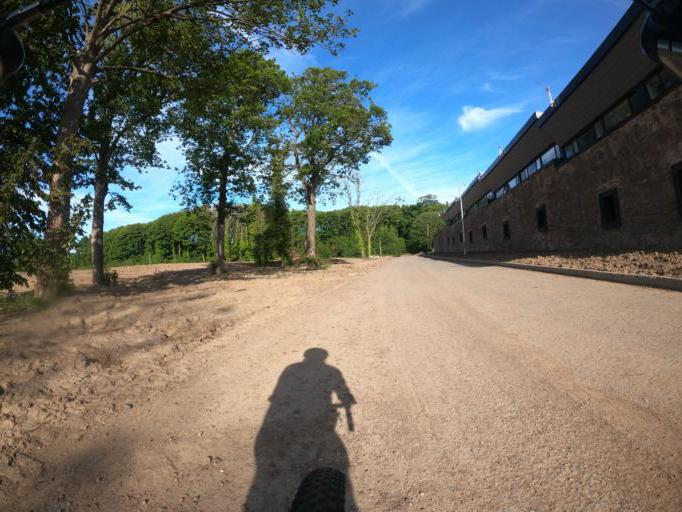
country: GB
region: Scotland
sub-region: Midlothian
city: Bonnyrigg
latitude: 55.9167
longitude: -3.1245
